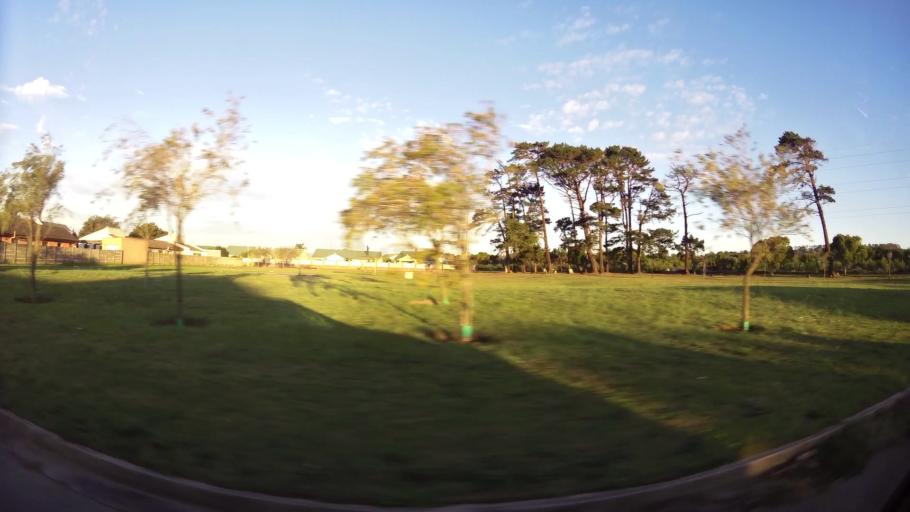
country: ZA
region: Eastern Cape
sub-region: Nelson Mandela Bay Metropolitan Municipality
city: Port Elizabeth
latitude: -33.9735
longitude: 25.5182
